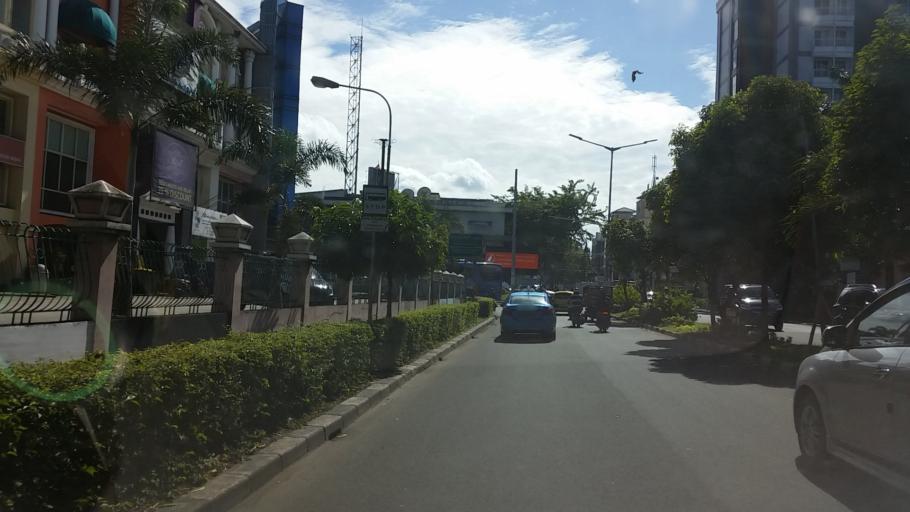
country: ID
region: Banten
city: South Tangerang
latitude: -6.2633
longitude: 106.7876
